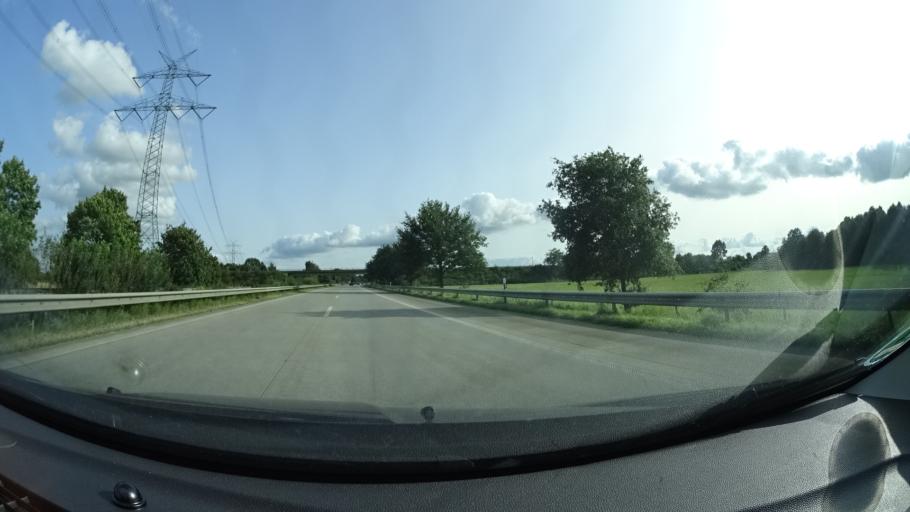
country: DE
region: Schleswig-Holstein
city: Klein Offenseth-Sparrieshoop
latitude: 53.7845
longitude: 9.7031
